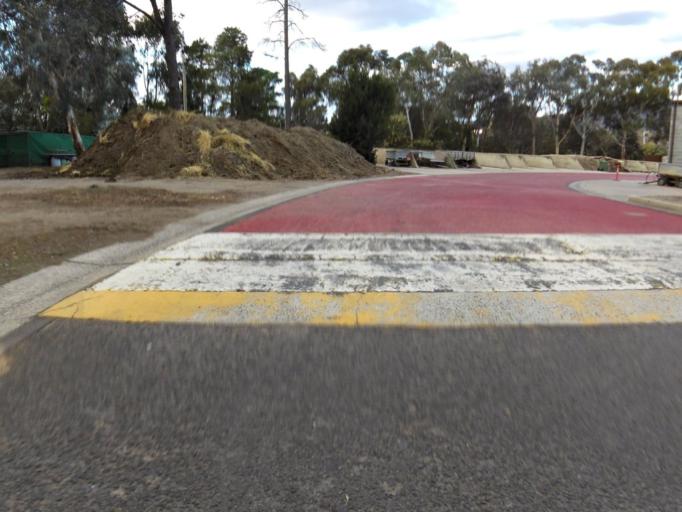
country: AU
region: Australian Capital Territory
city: Acton
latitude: -35.2707
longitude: 149.1128
